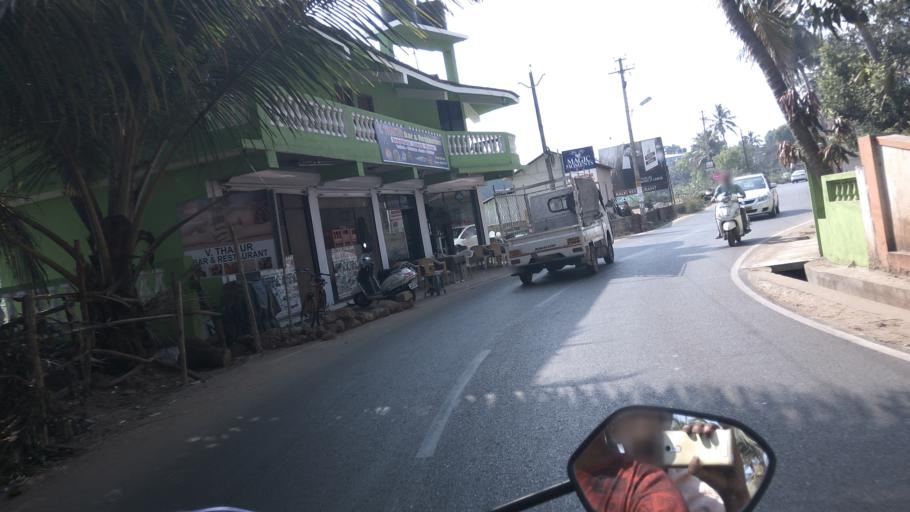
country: IN
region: Goa
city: Calangute
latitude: 15.5561
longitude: 73.7623
